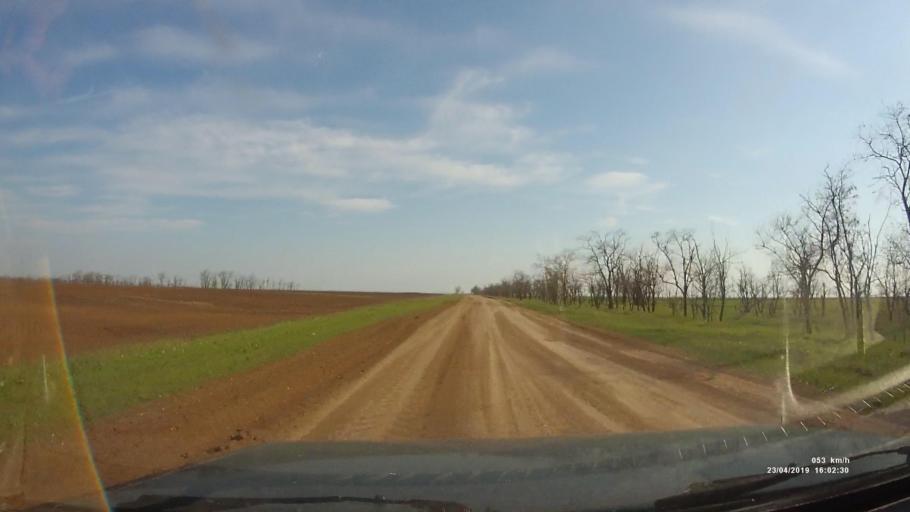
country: RU
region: Rostov
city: Remontnoye
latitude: 46.4939
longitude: 43.1070
